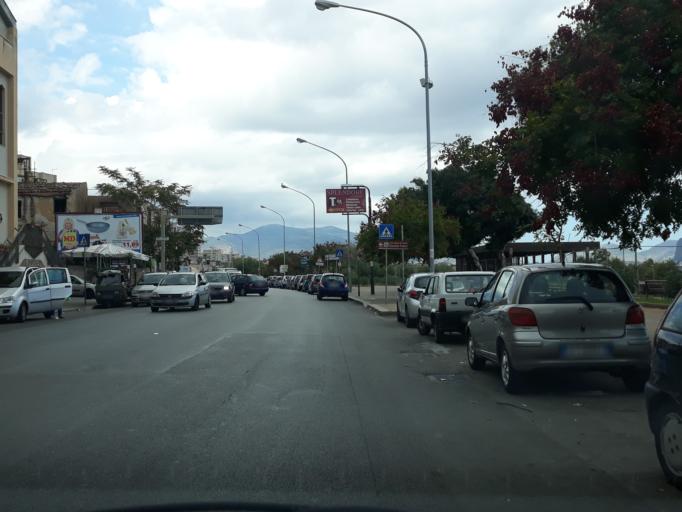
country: IT
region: Sicily
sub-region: Palermo
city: Ciaculli
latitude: 38.1054
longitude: 13.3888
